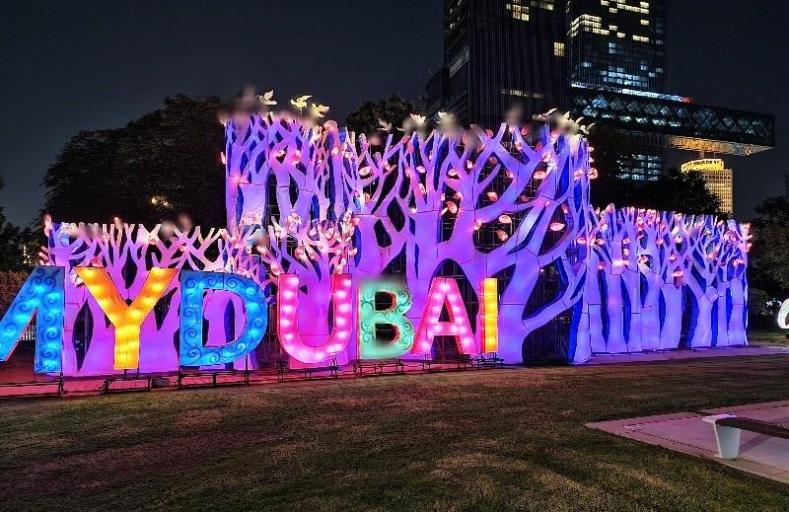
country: AE
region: Ash Shariqah
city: Sharjah
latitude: 25.2284
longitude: 55.2952
